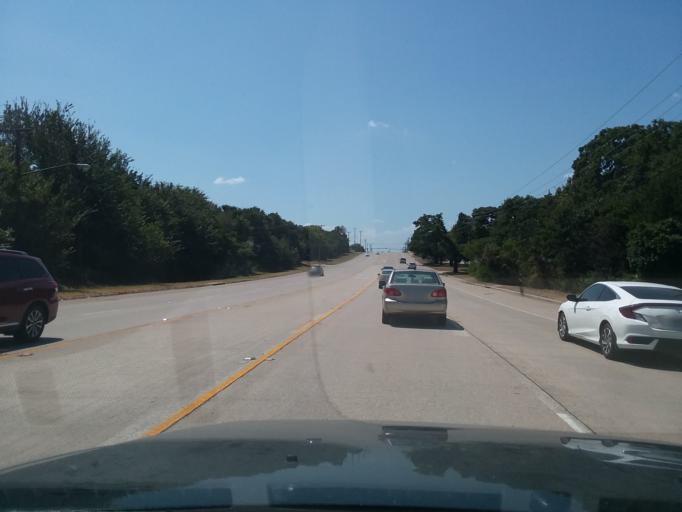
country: US
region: Texas
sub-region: Tarrant County
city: Euless
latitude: 32.8570
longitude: -97.1000
